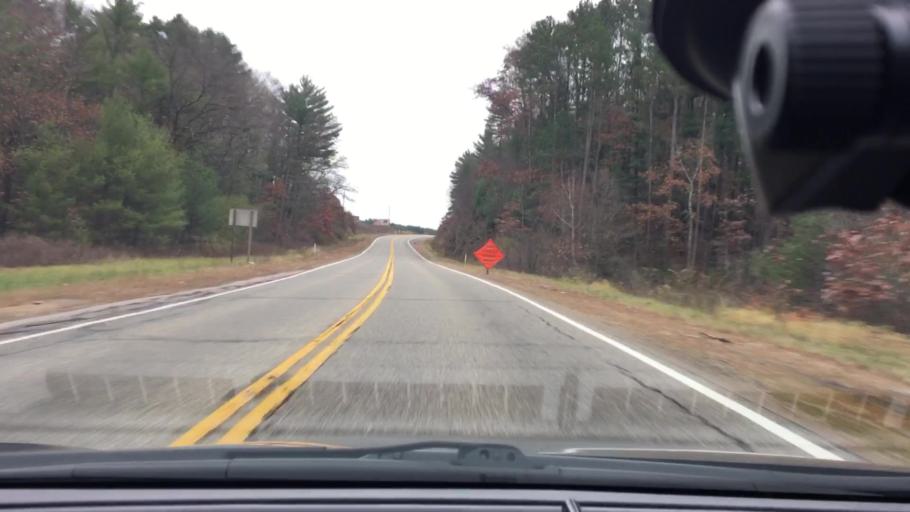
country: US
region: Wisconsin
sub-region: Columbia County
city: Wisconsin Dells
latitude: 43.6402
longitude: -89.8005
